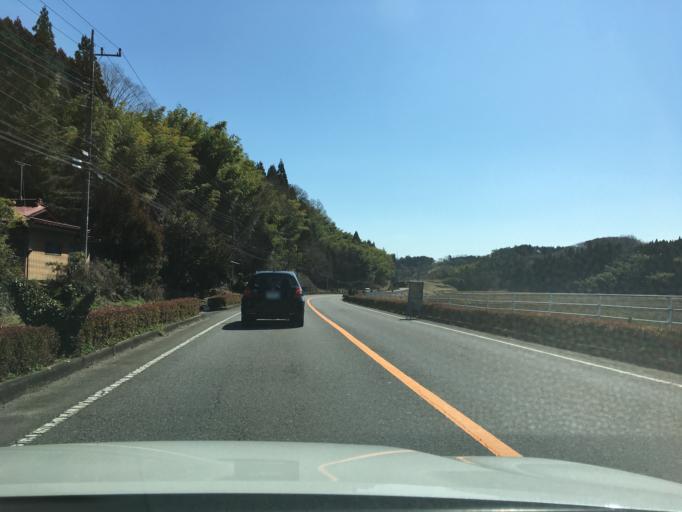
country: JP
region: Tochigi
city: Kuroiso
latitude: 37.0350
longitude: 140.1728
